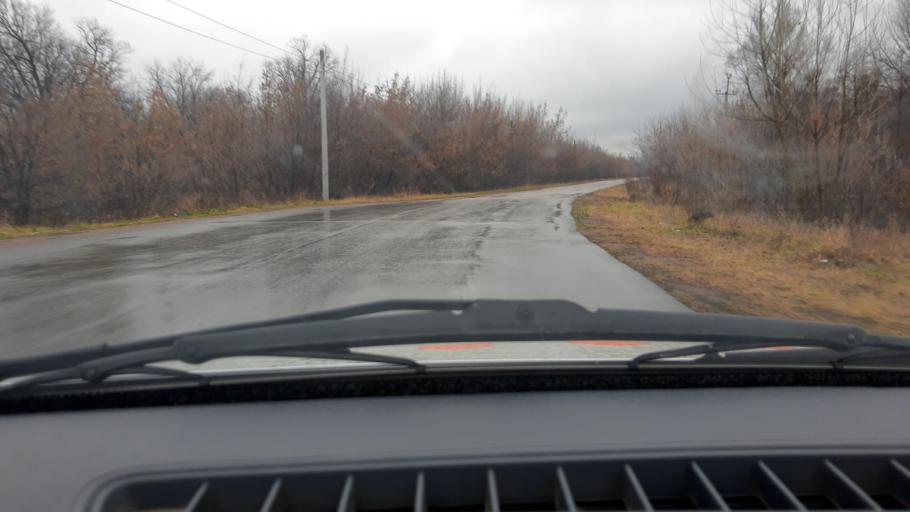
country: RU
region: Bashkortostan
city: Iglino
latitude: 54.8066
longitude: 56.1922
